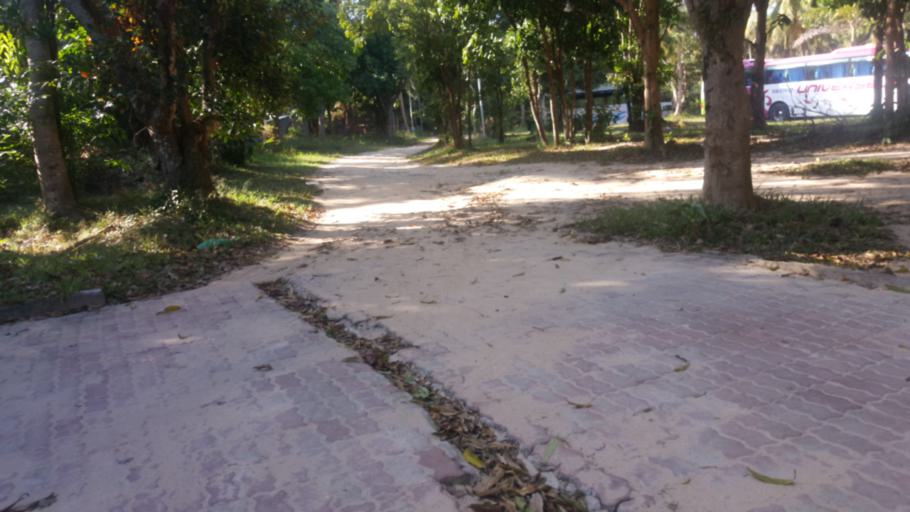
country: VN
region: Kien Giang
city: Duong GJong
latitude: 10.0559
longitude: 104.0348
